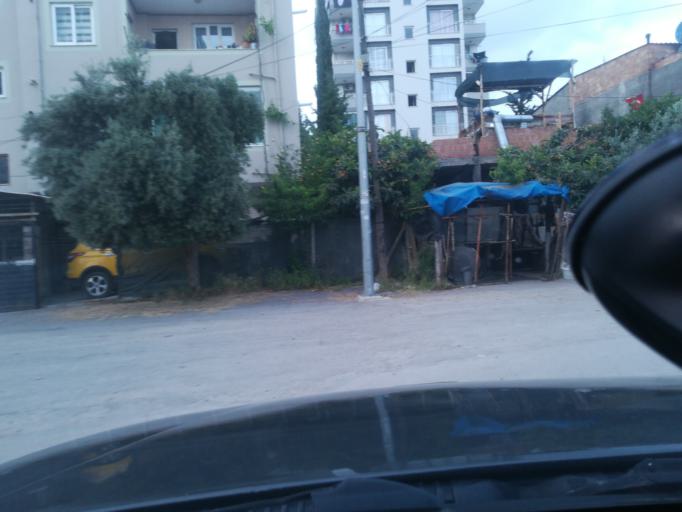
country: TR
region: Adana
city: Seyhan
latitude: 37.0130
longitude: 35.2711
